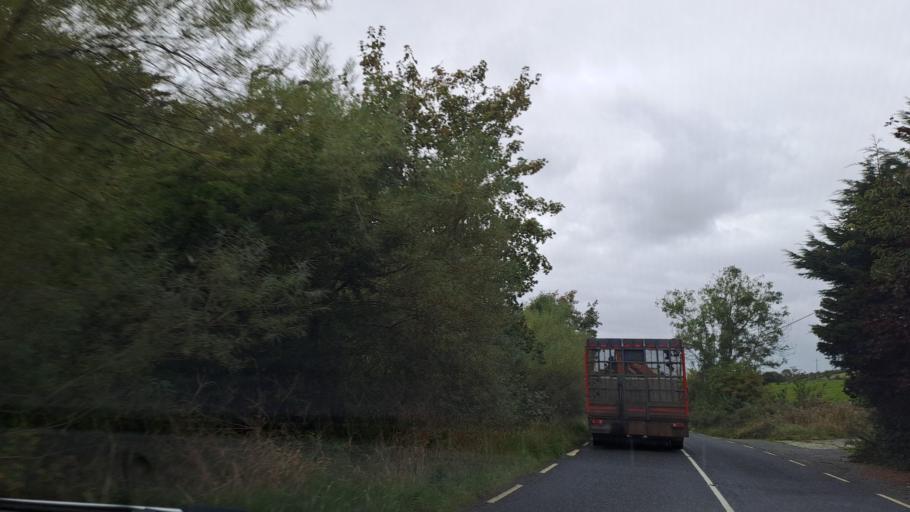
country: IE
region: Ulster
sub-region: County Monaghan
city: Castleblayney
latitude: 54.0919
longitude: -6.8399
